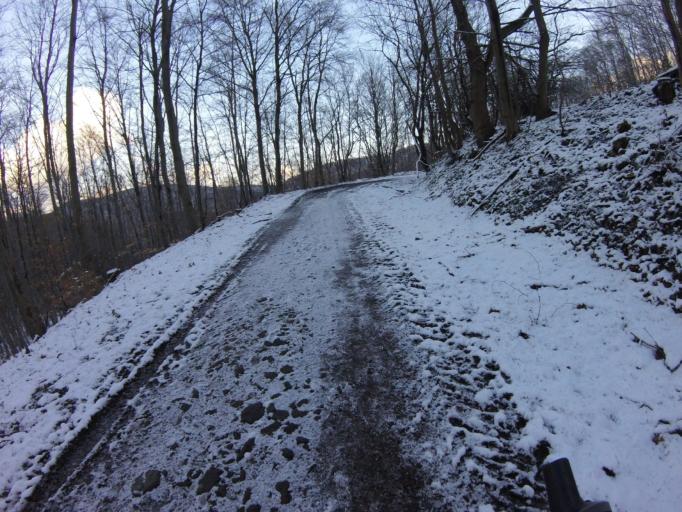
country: HU
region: Pest
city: Pilisszentkereszt
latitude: 47.7295
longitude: 18.8938
